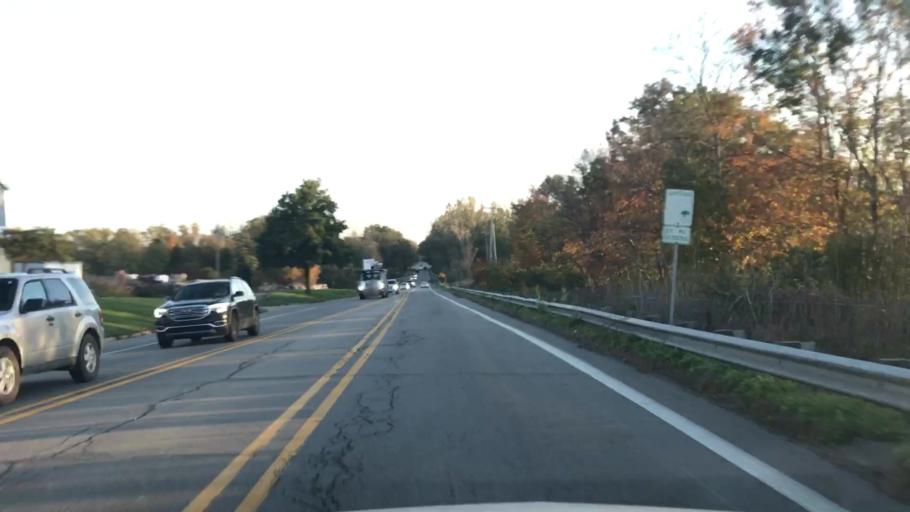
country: US
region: Michigan
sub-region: Macomb County
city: Shelby
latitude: 42.6605
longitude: -83.0735
